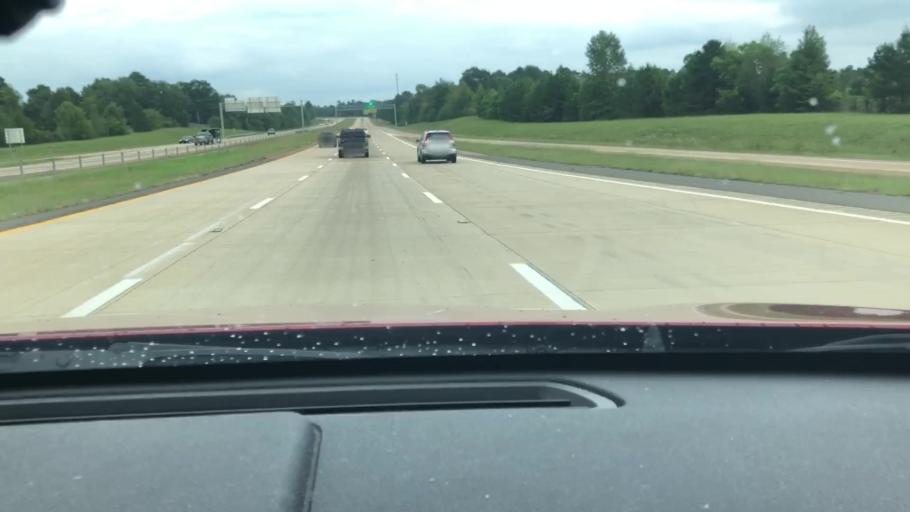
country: US
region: Texas
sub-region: Bowie County
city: Texarkana
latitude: 33.3951
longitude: -94.0122
